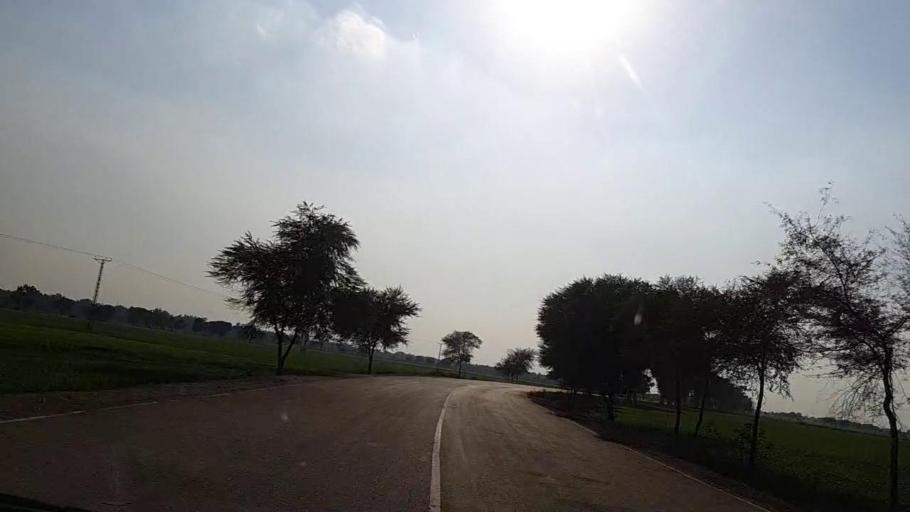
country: PK
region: Sindh
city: Sakrand
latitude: 26.1152
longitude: 68.2468
